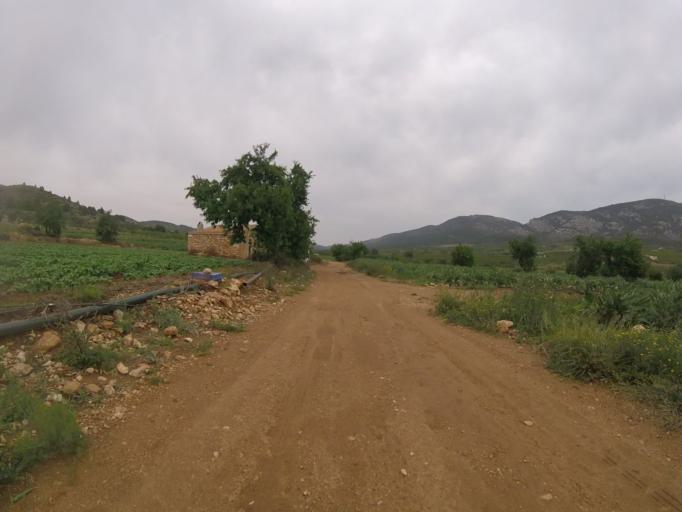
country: ES
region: Valencia
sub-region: Provincia de Castello
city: Alcala de Xivert
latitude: 40.2820
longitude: 0.2558
